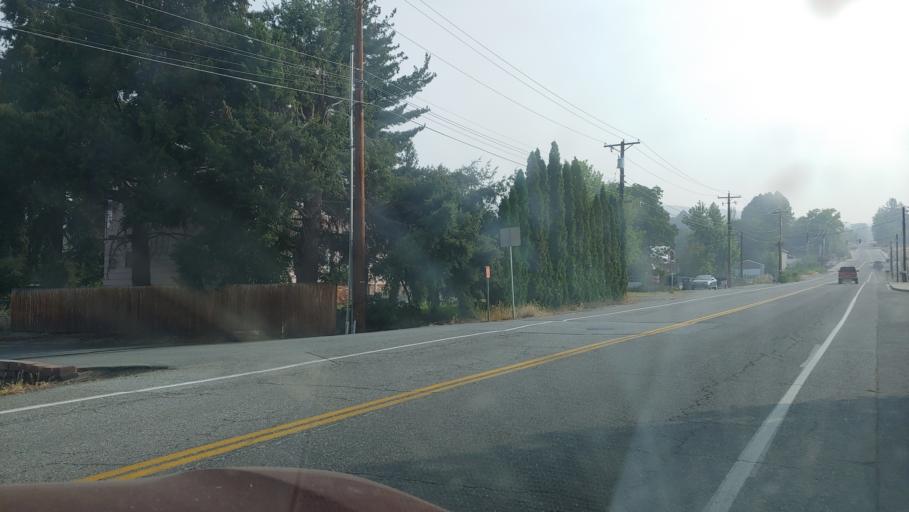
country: US
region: Washington
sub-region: Chelan County
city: Wenatchee
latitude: 47.4348
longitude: -120.3014
